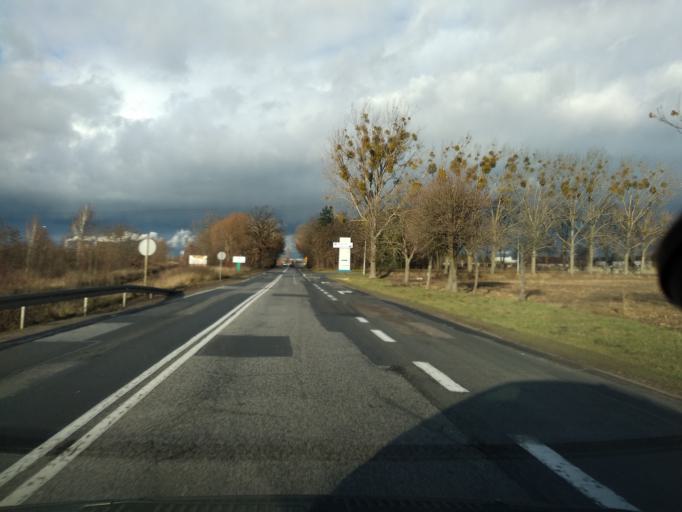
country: PL
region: Greater Poland Voivodeship
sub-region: Konin
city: Konin
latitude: 52.2613
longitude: 18.2680
